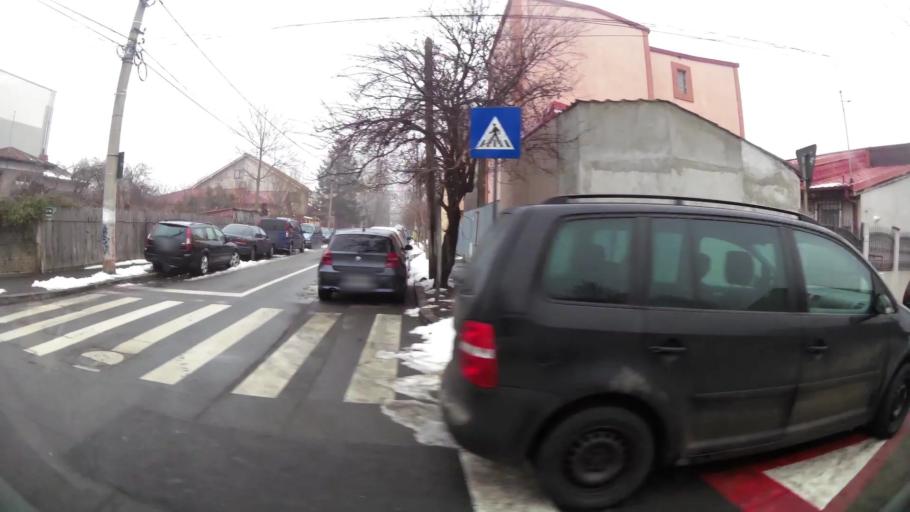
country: RO
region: Ilfov
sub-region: Comuna Chiajna
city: Rosu
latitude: 44.4753
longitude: 26.0419
